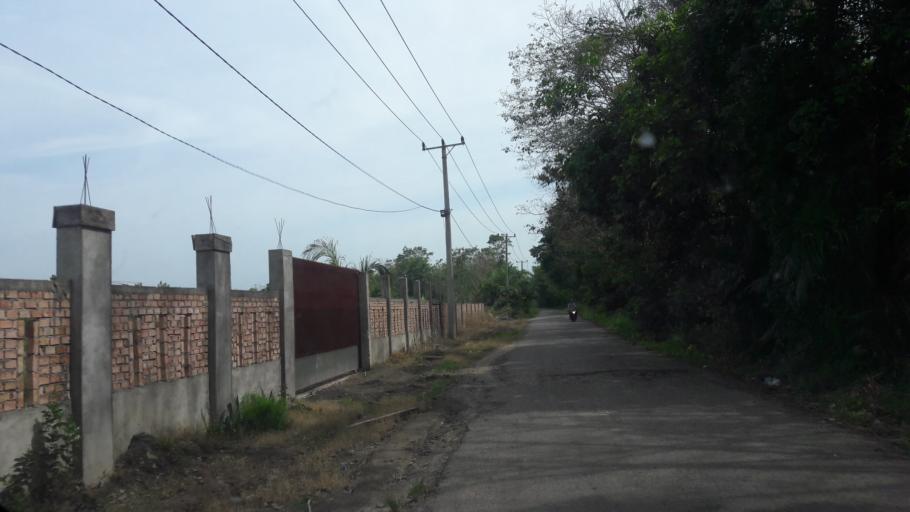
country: ID
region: South Sumatra
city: Gunungmenang
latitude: -3.2265
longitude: 104.1085
